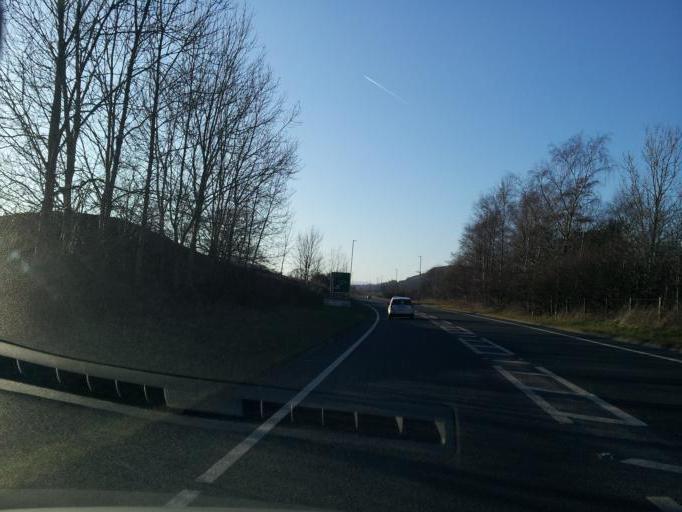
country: GB
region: England
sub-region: Cumbria
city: Kendal
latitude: 54.3671
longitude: -2.8024
